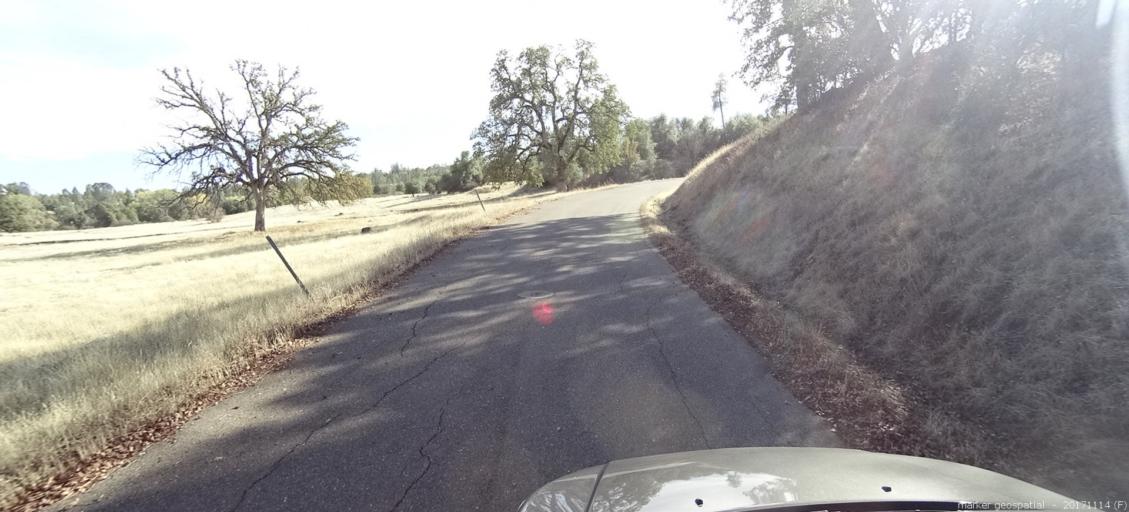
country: US
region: California
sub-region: Shasta County
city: Shasta
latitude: 40.3771
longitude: -122.5559
